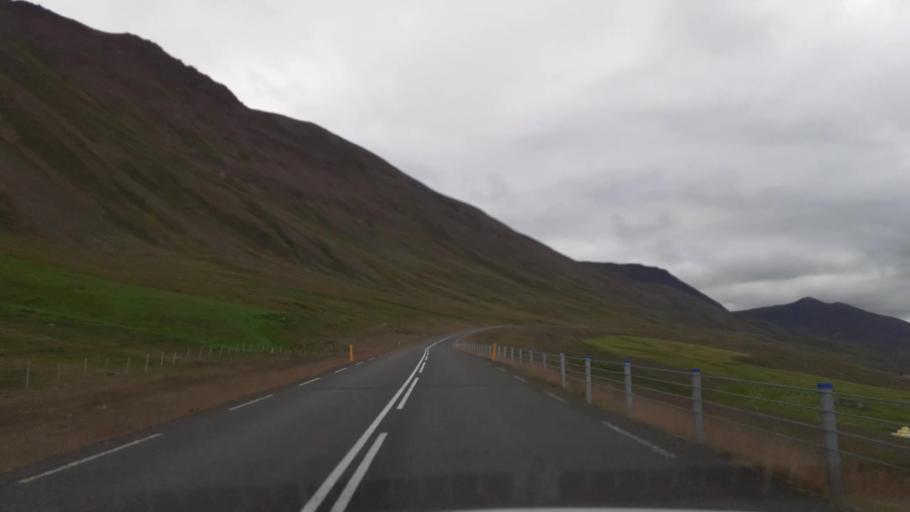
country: IS
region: Northeast
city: Akureyri
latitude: 65.8609
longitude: -18.0683
